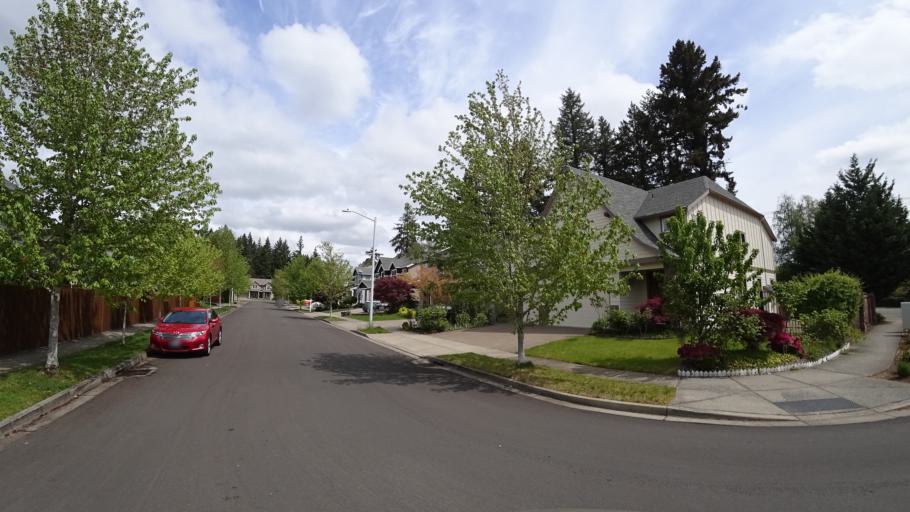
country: US
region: Oregon
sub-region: Washington County
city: Hillsboro
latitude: 45.5464
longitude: -122.9964
